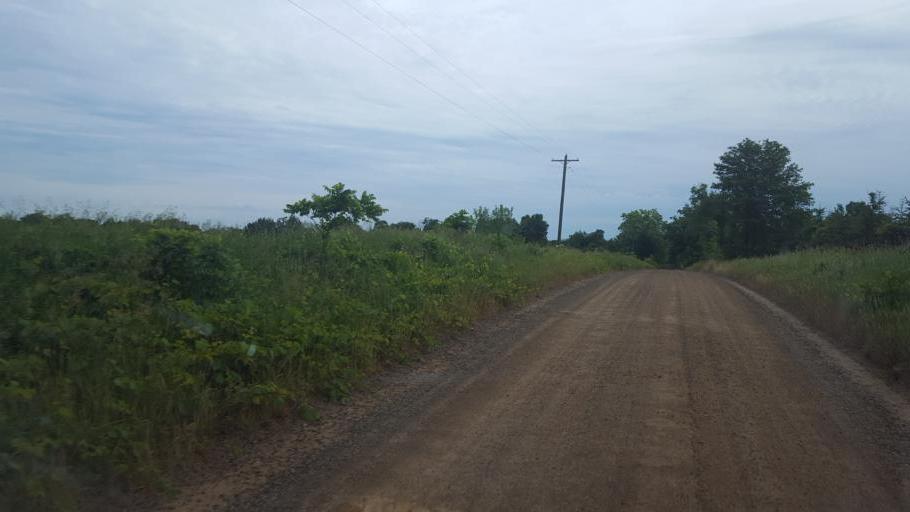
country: US
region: Michigan
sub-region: Eaton County
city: Charlotte
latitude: 42.6137
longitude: -84.8853
